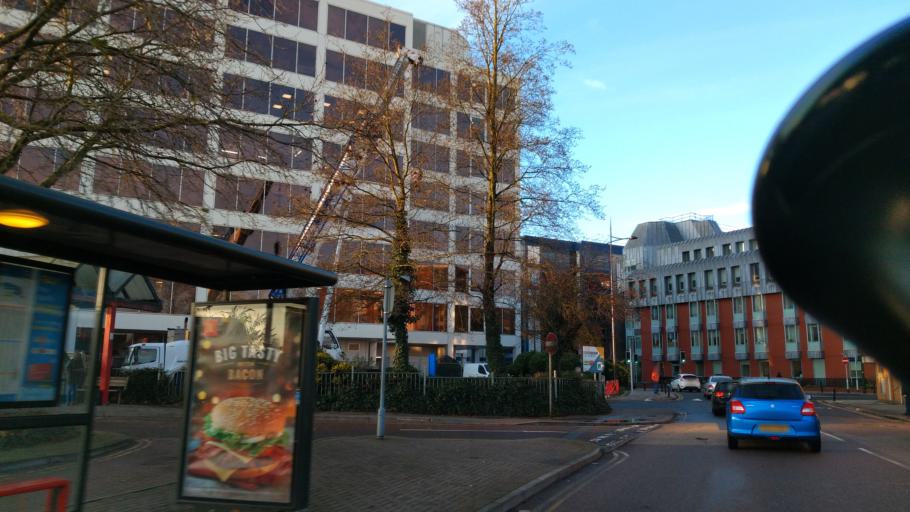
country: GB
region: England
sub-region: Borough of Swindon
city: Swindon
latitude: 51.5645
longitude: -1.7832
